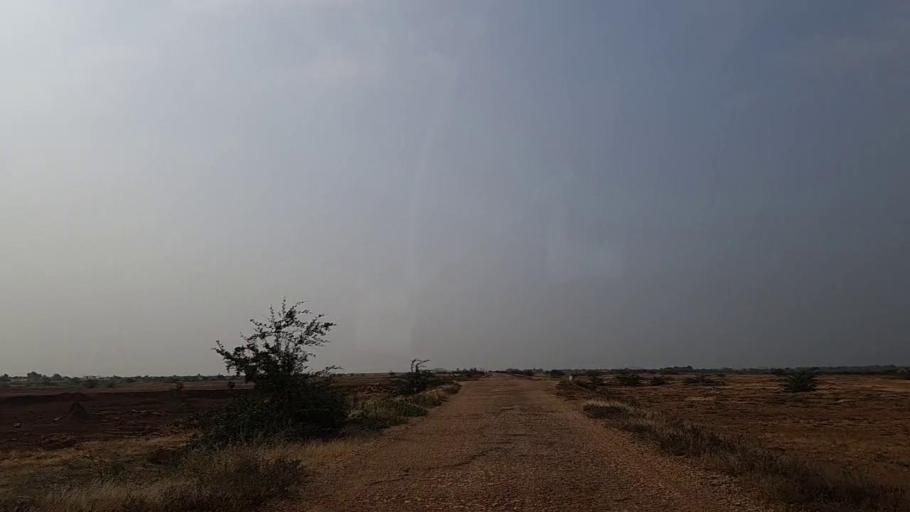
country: PK
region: Sindh
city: Thatta
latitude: 24.7351
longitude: 67.8385
